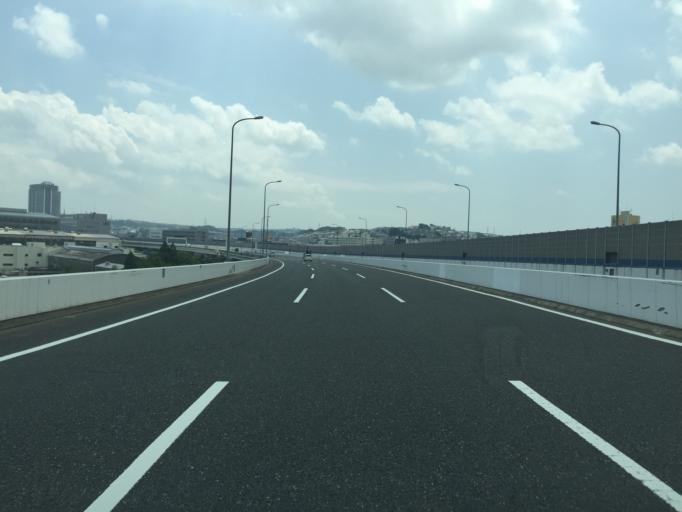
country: JP
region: Kanagawa
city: Yokohama
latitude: 35.3963
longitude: 139.6168
